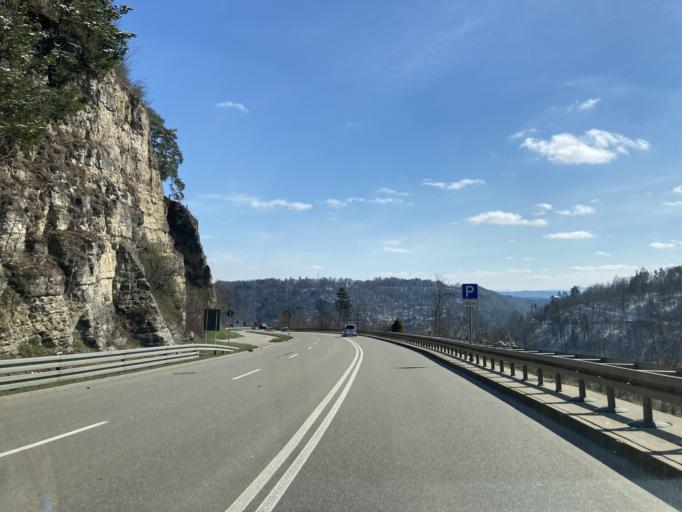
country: DE
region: Baden-Wuerttemberg
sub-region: Freiburg Region
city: Oberndorf
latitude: 48.2907
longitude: 8.5617
